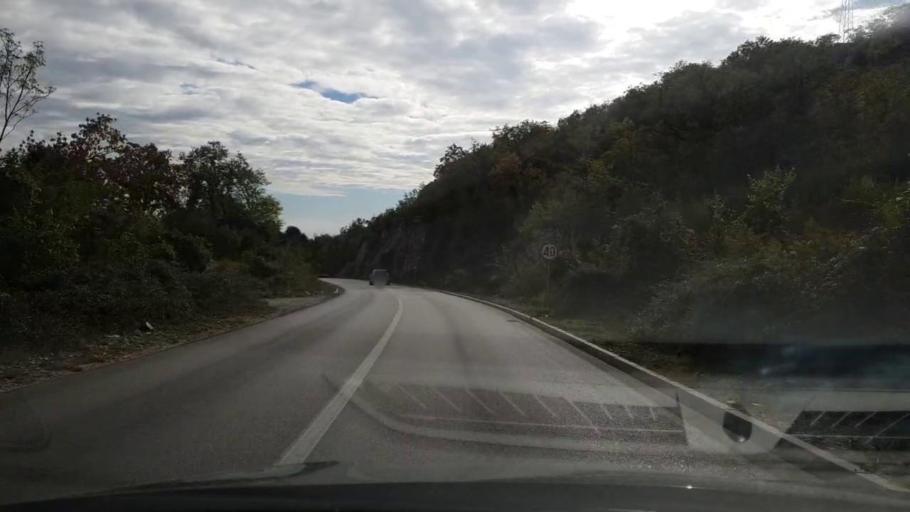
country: ME
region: Herceg Novi
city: Herceg-Novi
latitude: 42.4757
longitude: 18.5289
